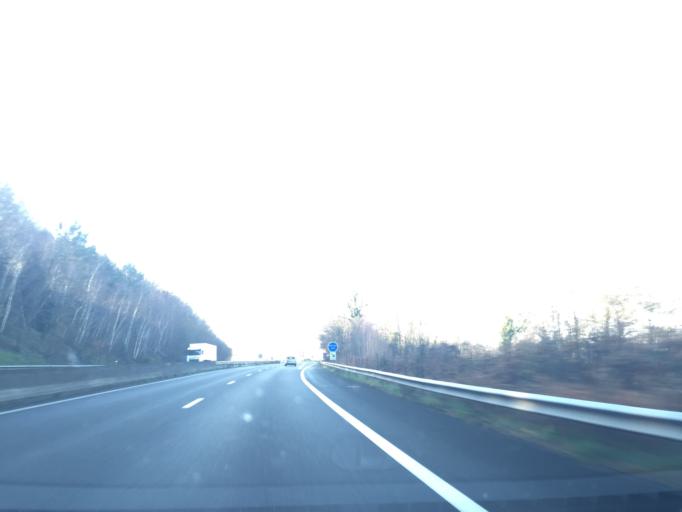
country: FR
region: Limousin
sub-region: Departement de la Correze
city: Donzenac
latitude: 45.2465
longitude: 1.5231
